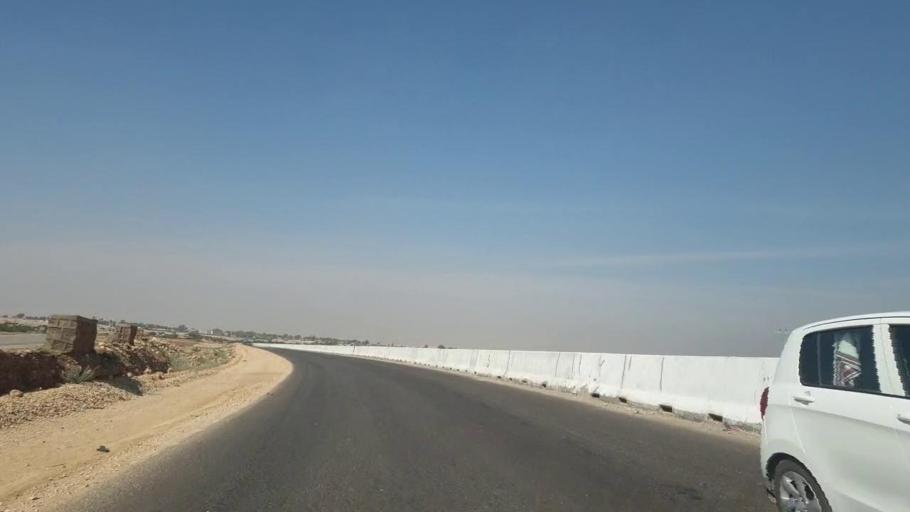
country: PK
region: Sindh
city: Matiari
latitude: 25.6561
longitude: 68.3002
